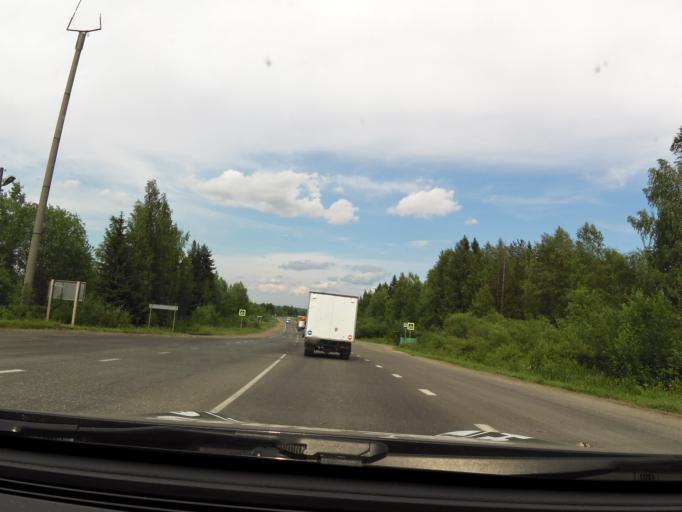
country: RU
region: Kirov
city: Stulovo
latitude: 58.7002
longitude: 50.0900
